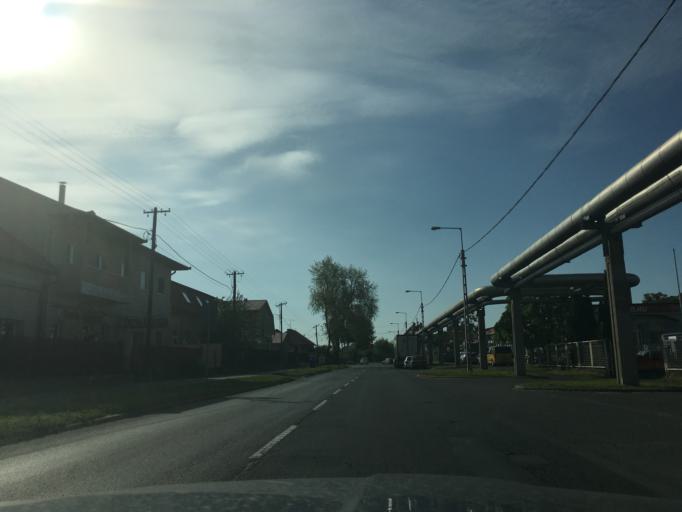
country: HU
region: Hajdu-Bihar
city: Debrecen
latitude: 47.5140
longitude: 21.6359
